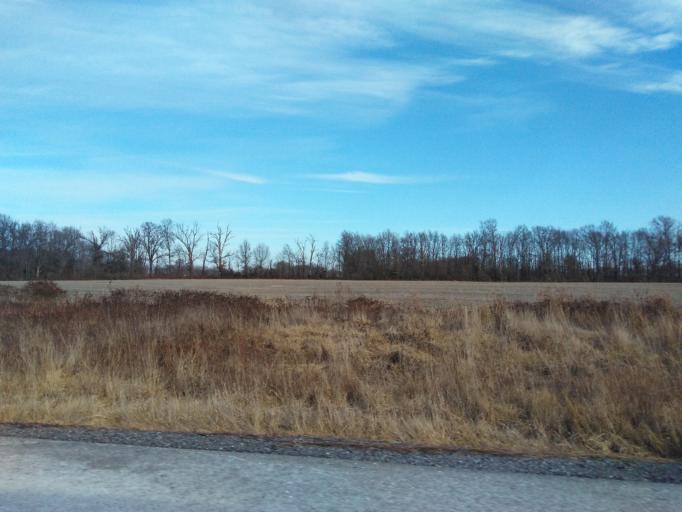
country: US
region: Illinois
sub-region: Jefferson County
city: Ina
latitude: 38.2077
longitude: -88.9110
